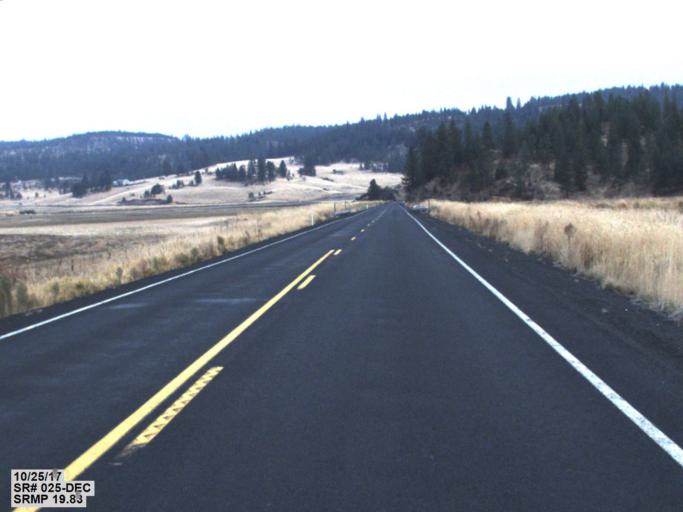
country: US
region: Washington
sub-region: Lincoln County
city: Davenport
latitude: 47.8919
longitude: -118.2703
